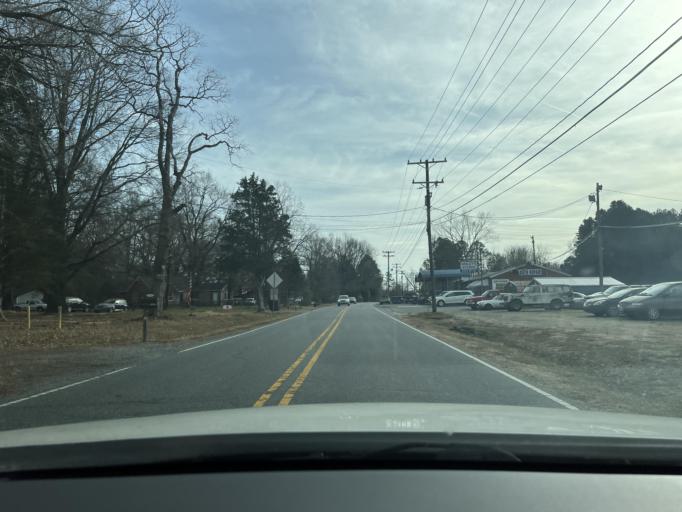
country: US
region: North Carolina
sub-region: Guilford County
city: Pleasant Garden
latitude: 36.0050
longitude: -79.7779
